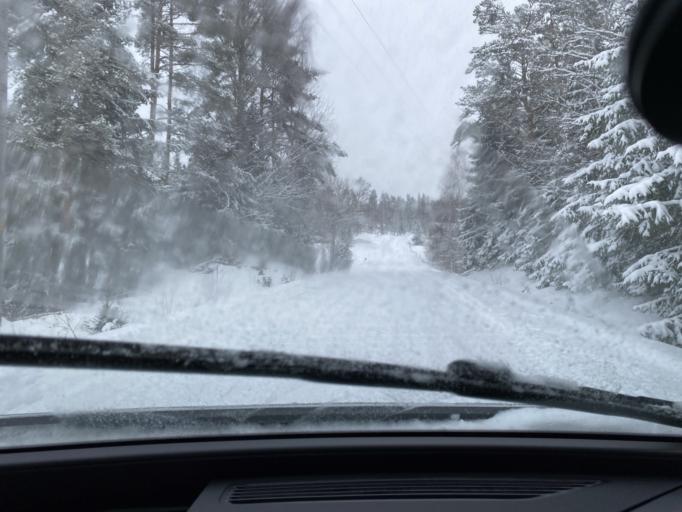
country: FI
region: Haeme
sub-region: Forssa
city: Humppila
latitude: 61.0151
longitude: 23.3092
